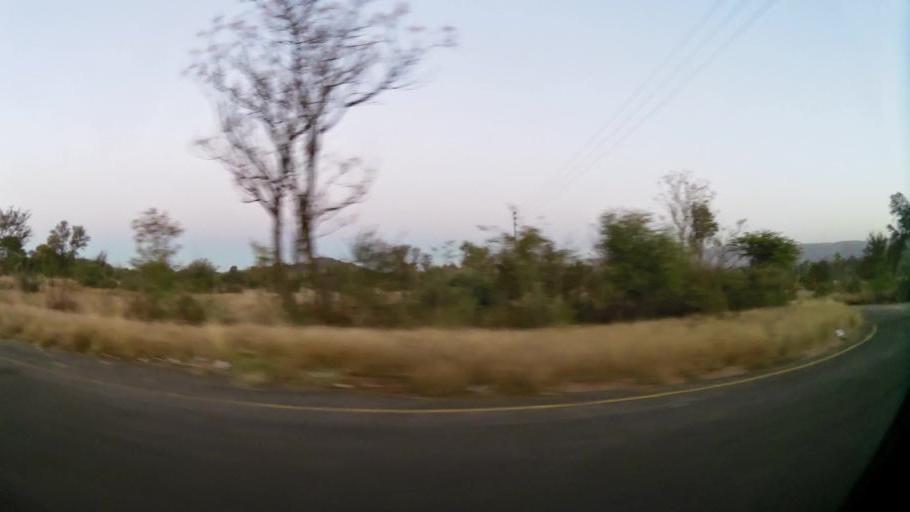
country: ZA
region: North-West
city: Ga-Rankuwa
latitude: -25.6371
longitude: 27.9524
